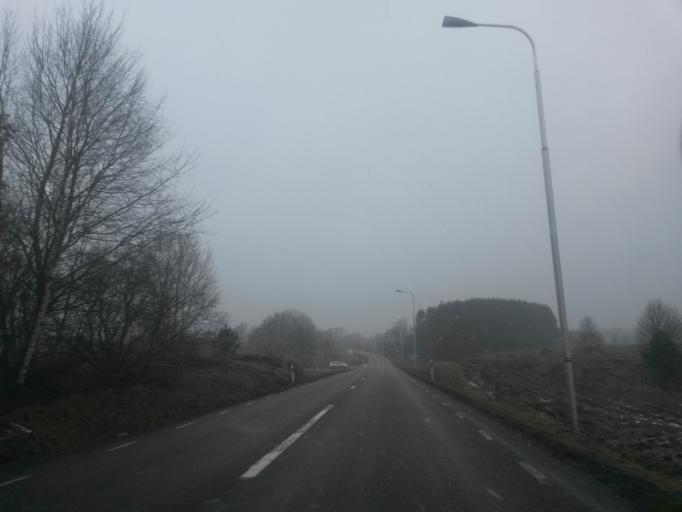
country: SE
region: Vaestra Goetaland
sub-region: Vanersborgs Kommun
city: Vargon
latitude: 58.2442
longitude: 12.4240
